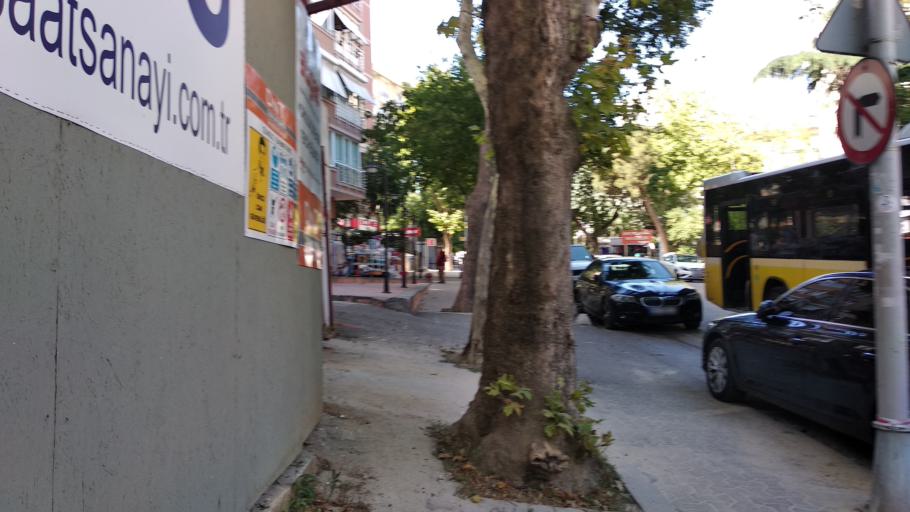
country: TR
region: Istanbul
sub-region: Atasehir
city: Atasehir
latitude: 40.9569
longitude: 29.0947
